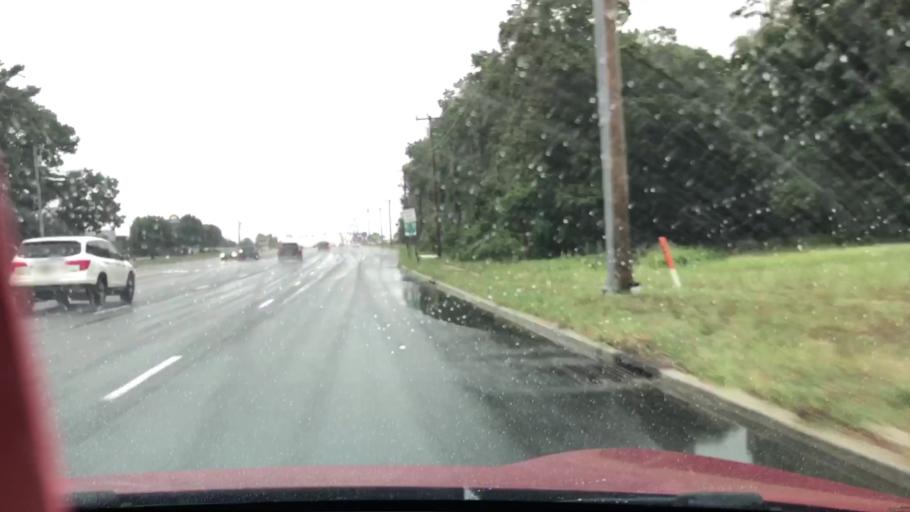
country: US
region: New Jersey
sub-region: Atlantic County
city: Northfield
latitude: 39.3978
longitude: -74.5608
